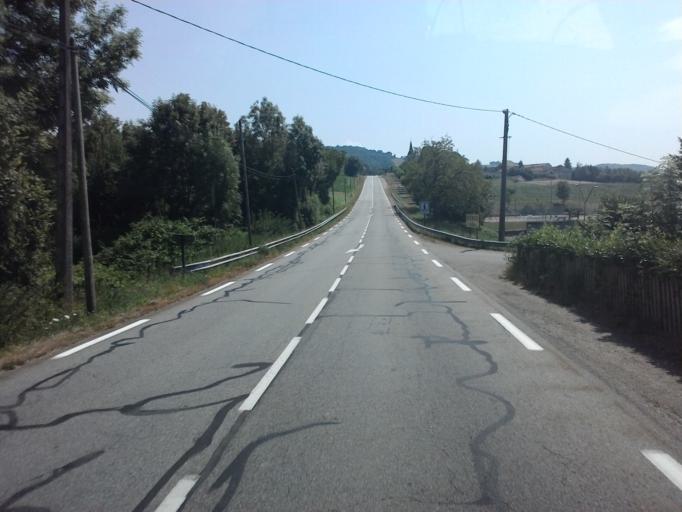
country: FR
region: Rhone-Alpes
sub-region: Departement de l'Isere
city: Montferrat
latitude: 45.4942
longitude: 5.5931
